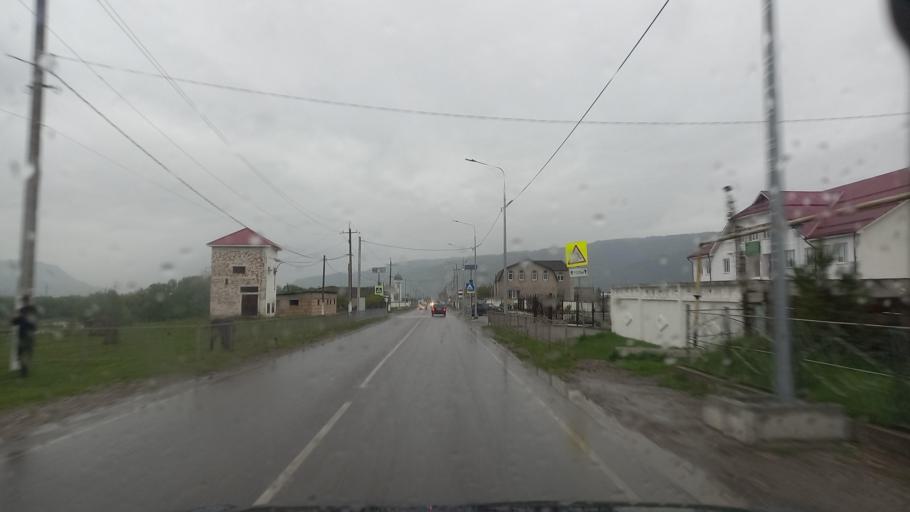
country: RU
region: Kabardino-Balkariya
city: Zhankhoteko
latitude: 43.5892
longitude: 43.2040
